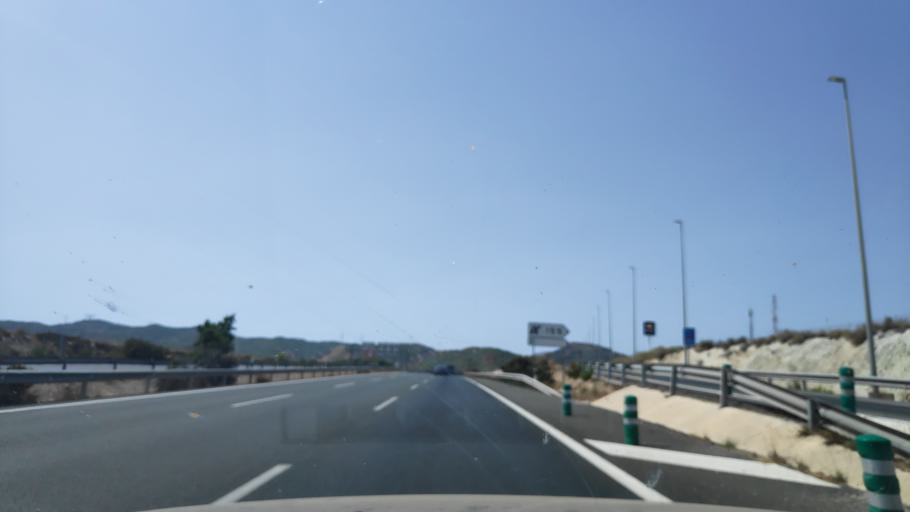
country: ES
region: Murcia
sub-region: Murcia
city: Murcia
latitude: 37.8822
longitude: -1.1341
